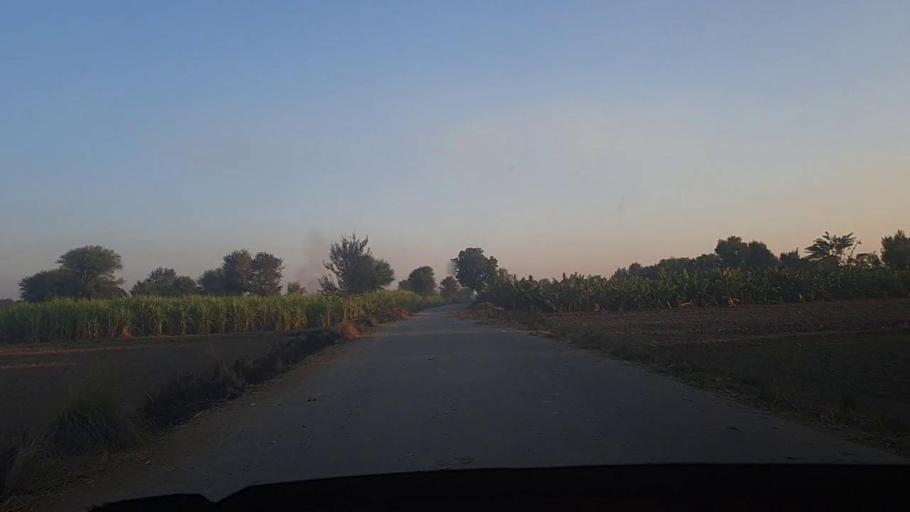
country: PK
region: Sindh
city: Sobhadero
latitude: 27.3478
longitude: 68.3754
